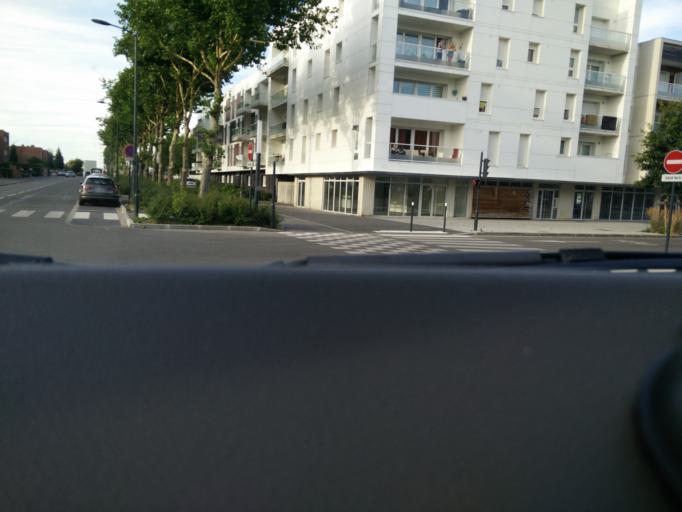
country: FR
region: Nord-Pas-de-Calais
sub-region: Departement du Pas-de-Calais
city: Lens
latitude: 50.4441
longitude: 2.8280
